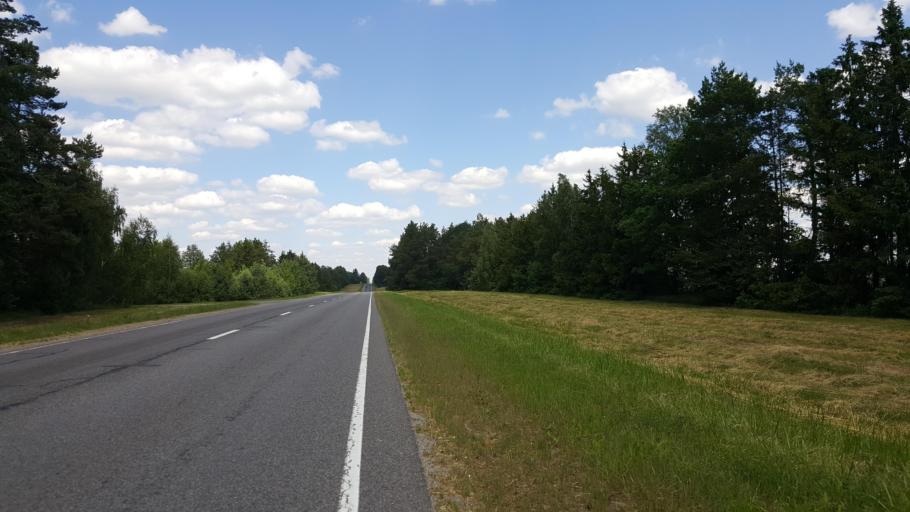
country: BY
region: Brest
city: Kamyanyets
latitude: 52.4498
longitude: 23.7836
